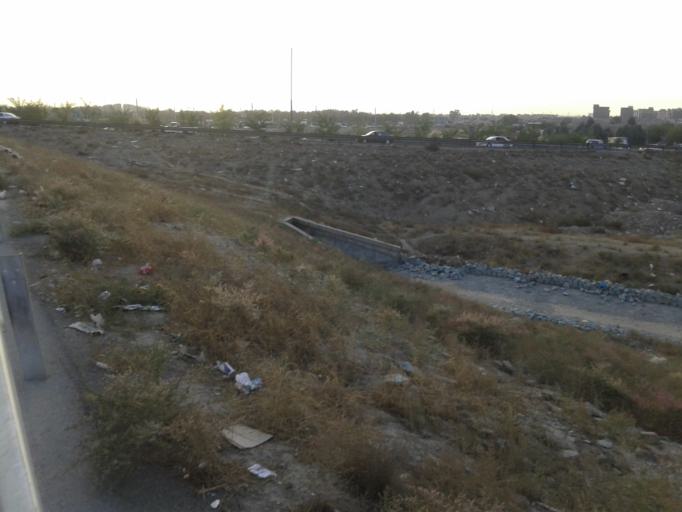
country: IR
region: Tehran
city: Eslamshahr
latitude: 35.6520
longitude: 51.2755
